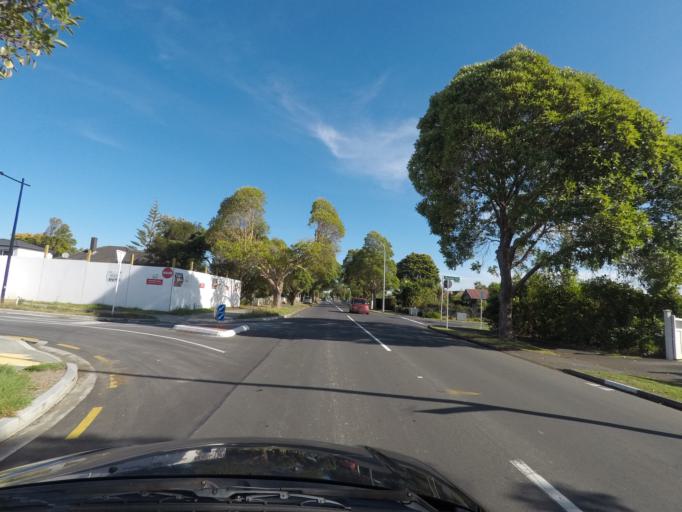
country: NZ
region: Auckland
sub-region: Auckland
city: Rosebank
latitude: -36.9034
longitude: 174.6967
